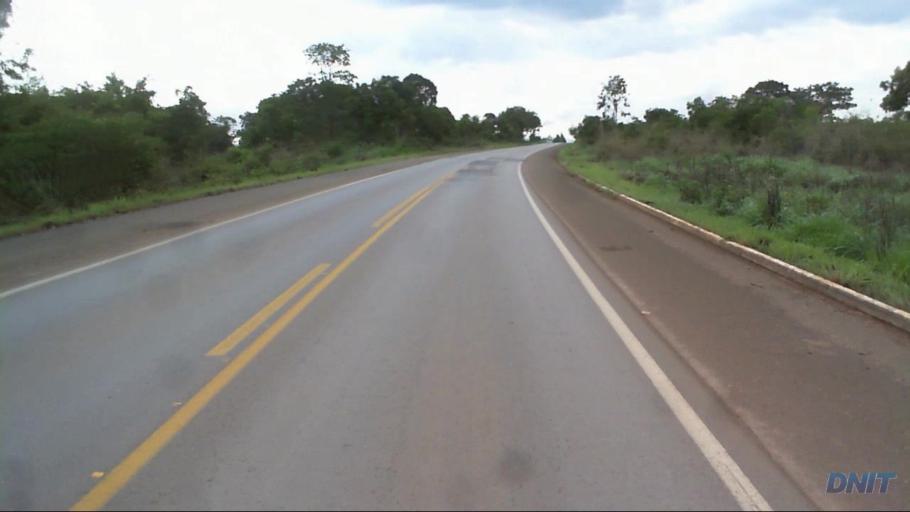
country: BR
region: Goias
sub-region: Uruacu
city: Uruacu
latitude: -14.7263
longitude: -49.0953
